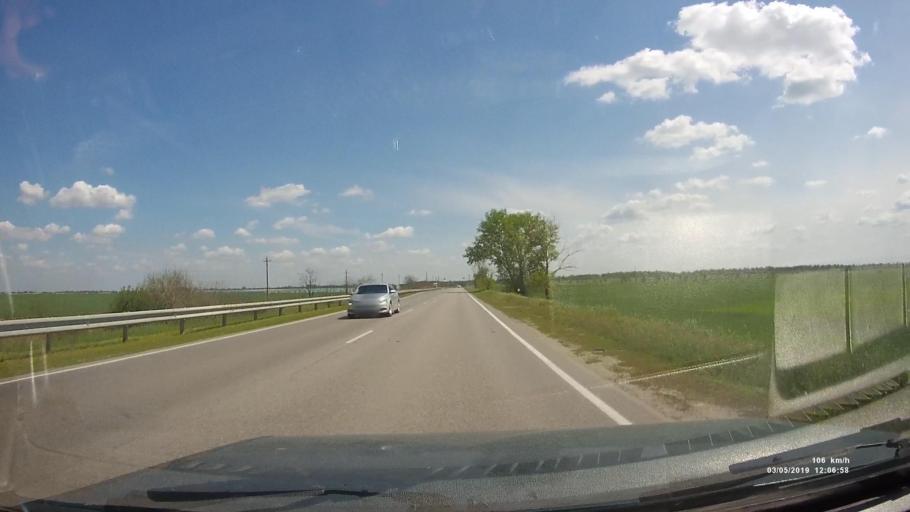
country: RU
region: Rostov
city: Bagayevskaya
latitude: 47.2852
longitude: 40.4638
